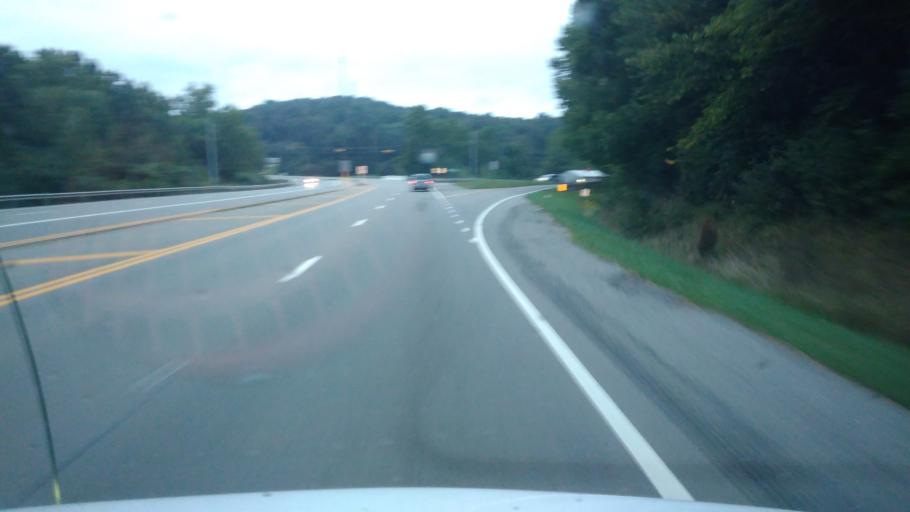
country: US
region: Ohio
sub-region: Ross County
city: Chillicothe
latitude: 39.2486
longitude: -82.9826
